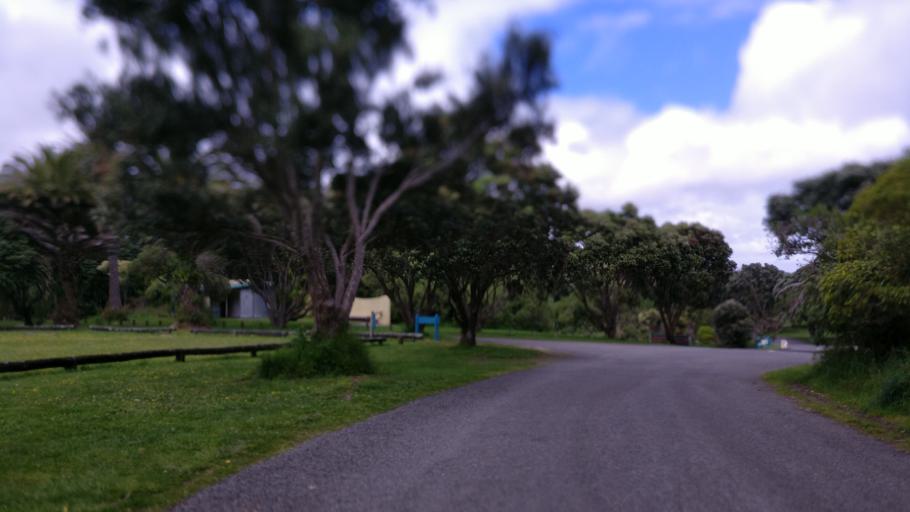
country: NZ
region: Wellington
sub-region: Kapiti Coast District
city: Paraparaumu
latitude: -40.9734
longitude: 174.9623
